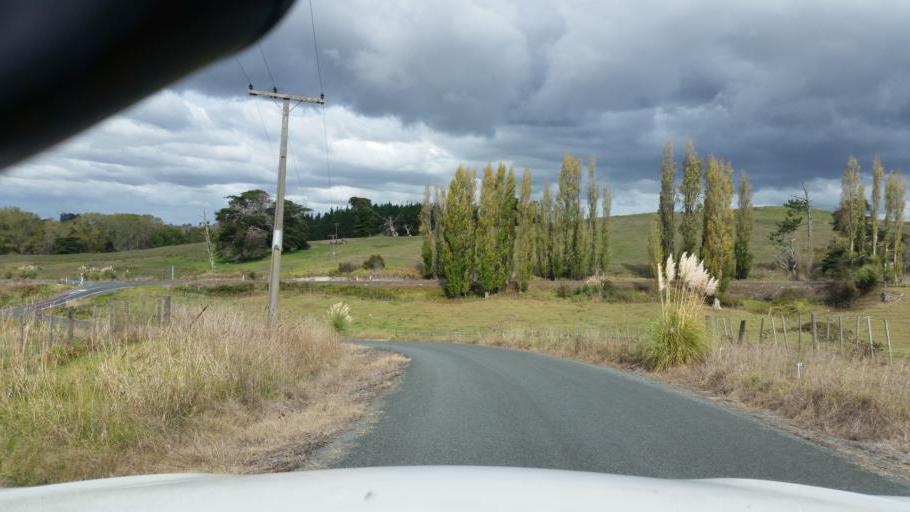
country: NZ
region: Northland
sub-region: Whangarei
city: Ruakaka
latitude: -36.1096
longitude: 174.2776
